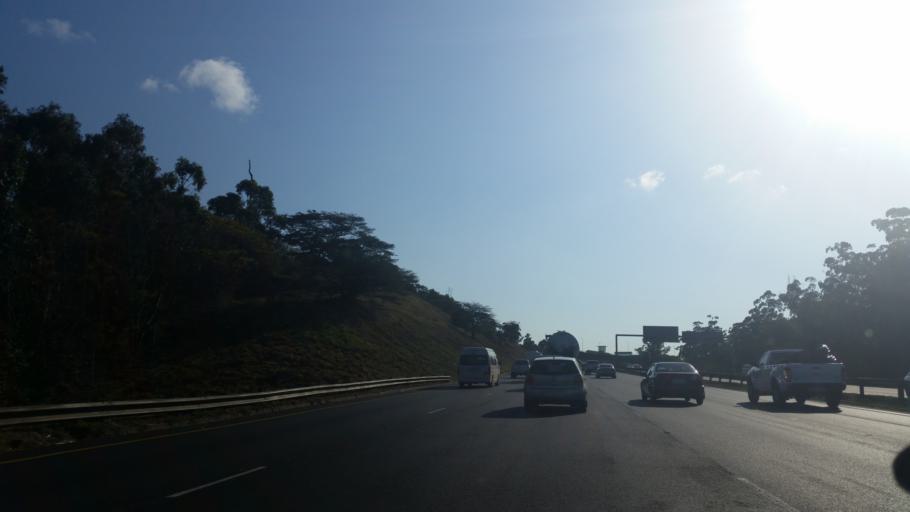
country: ZA
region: KwaZulu-Natal
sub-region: eThekwini Metropolitan Municipality
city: Berea
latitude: -29.8345
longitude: 30.9595
